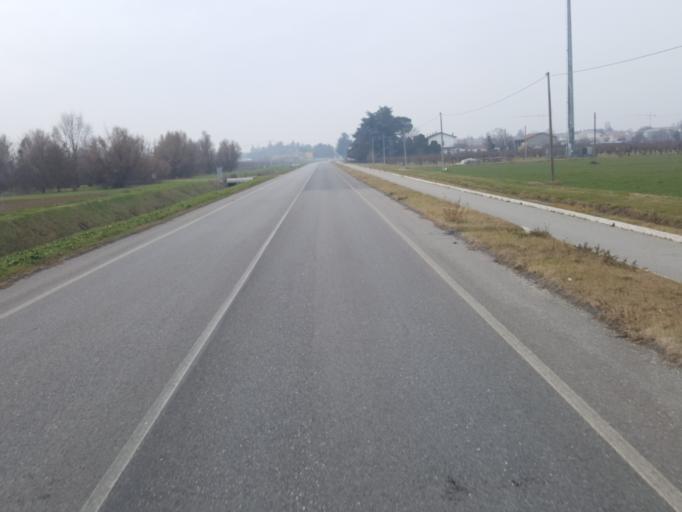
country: IT
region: Emilia-Romagna
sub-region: Forli-Cesena
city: Cesena
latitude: 44.1561
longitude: 12.2783
